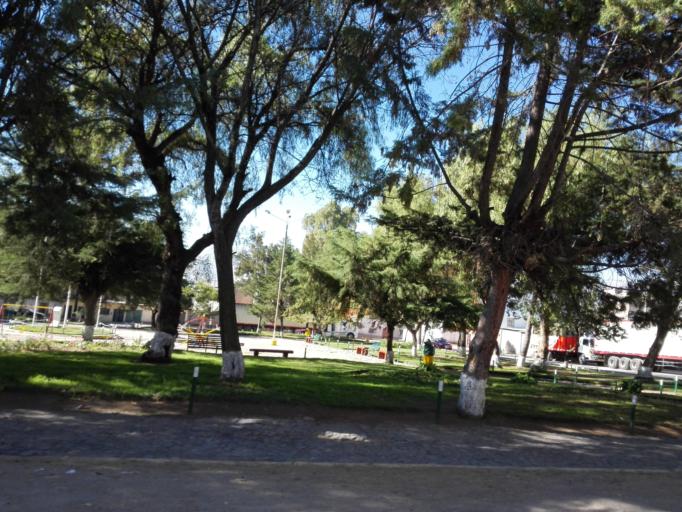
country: PE
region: Ayacucho
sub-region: Provincia de Huamanga
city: Ayacucho
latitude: -13.1544
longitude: -74.2159
